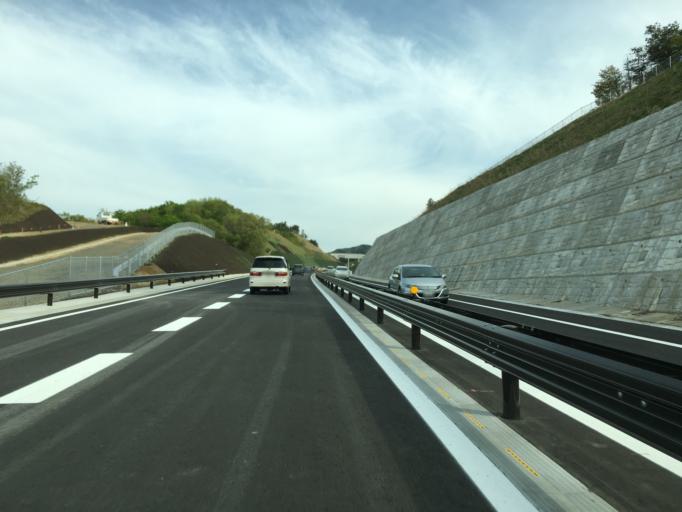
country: JP
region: Fukushima
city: Hobaramachi
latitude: 37.7973
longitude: 140.5459
